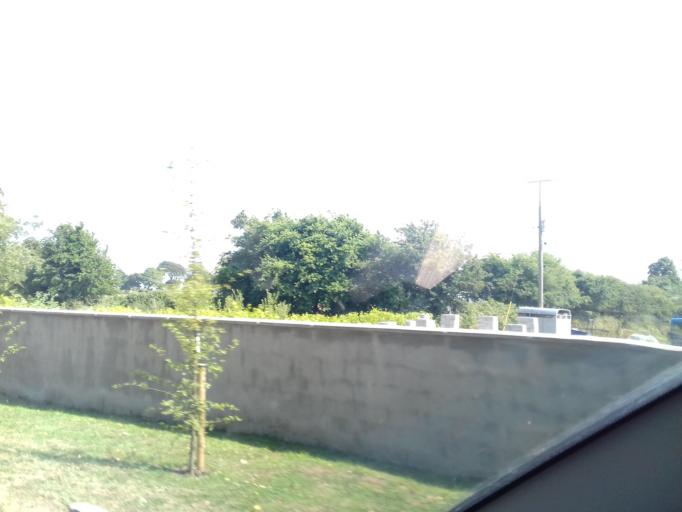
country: IE
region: Leinster
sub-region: An Mhi
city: Stamullin
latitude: 53.6006
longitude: -6.3038
